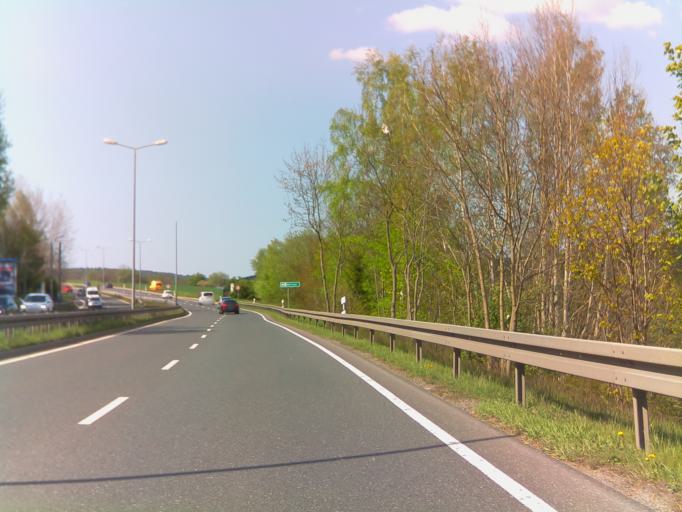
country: DE
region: Saxony
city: Plauen
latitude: 50.5009
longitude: 12.1718
